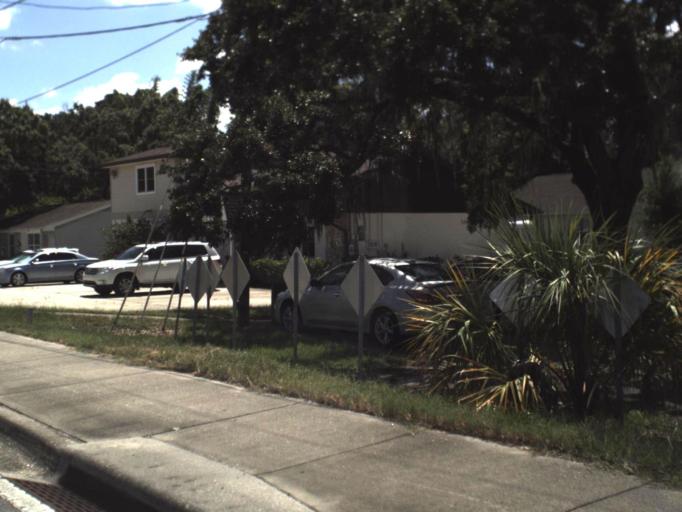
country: US
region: Florida
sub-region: Pinellas County
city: Oldsmar
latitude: 28.0379
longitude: -82.6670
